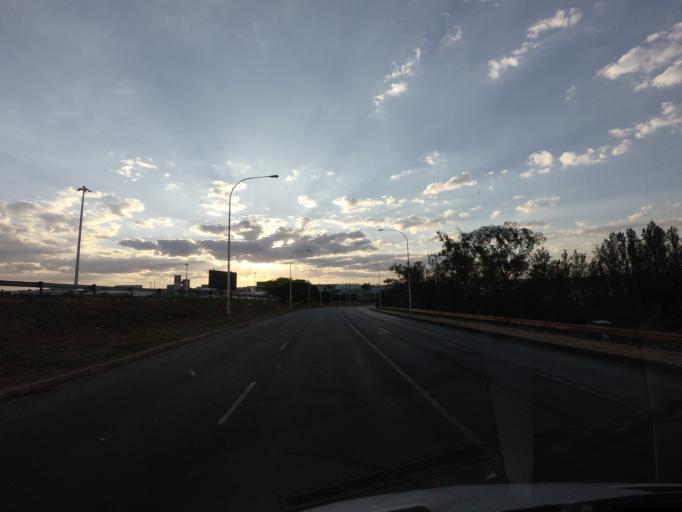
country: ZA
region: Gauteng
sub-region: City of Johannesburg Metropolitan Municipality
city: Modderfontein
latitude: -26.1305
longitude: 28.2232
